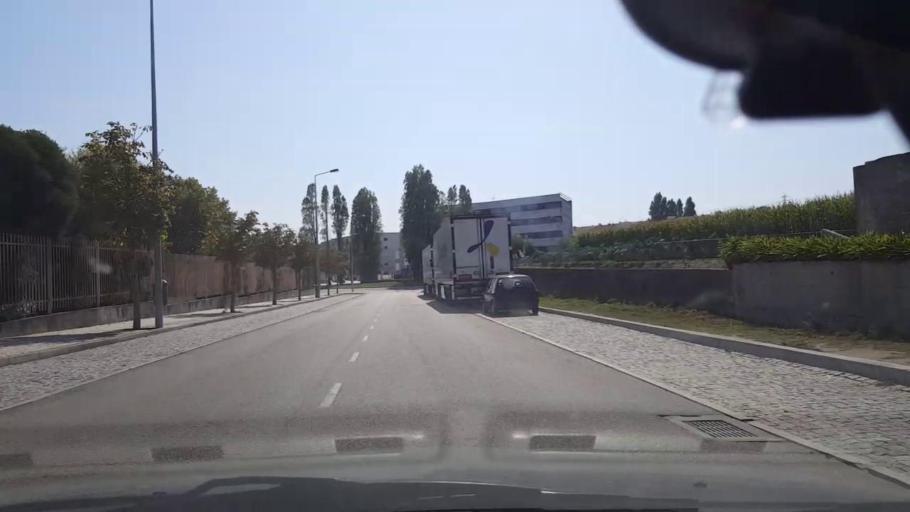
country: PT
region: Porto
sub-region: Vila do Conde
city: Vila do Conde
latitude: 41.3600
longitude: -8.7325
